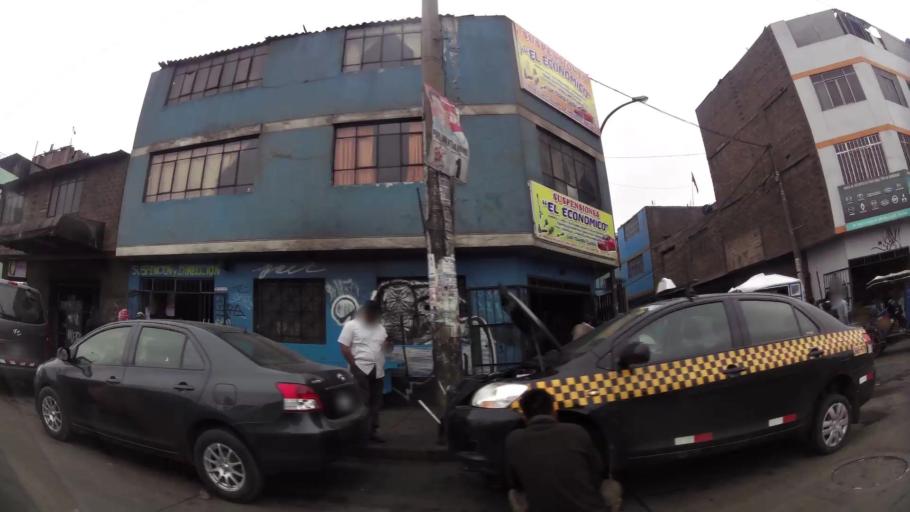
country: PE
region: Lima
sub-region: Lima
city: San Luis
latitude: -12.0625
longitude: -77.0033
